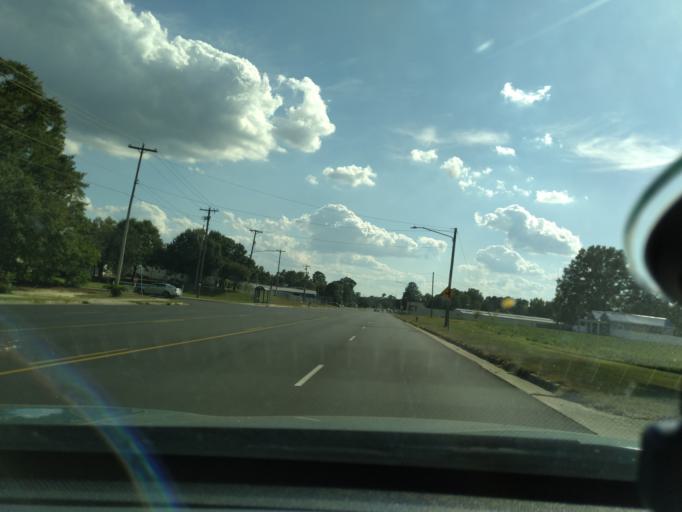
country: US
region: North Carolina
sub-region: Nash County
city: Rocky Mount
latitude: 35.9211
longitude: -77.8247
